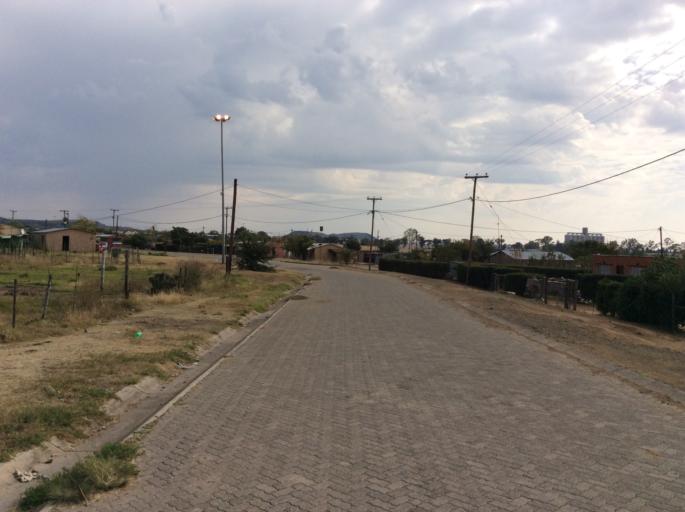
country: ZA
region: Orange Free State
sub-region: Xhariep District Municipality
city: Dewetsdorp
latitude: -29.5800
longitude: 26.6897
